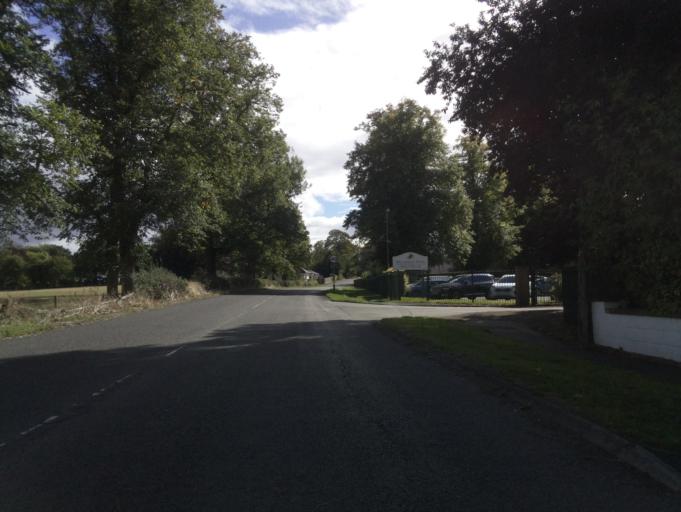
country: GB
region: England
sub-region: Leicestershire
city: Ashby de la Zouch
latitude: 52.7383
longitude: -1.4822
